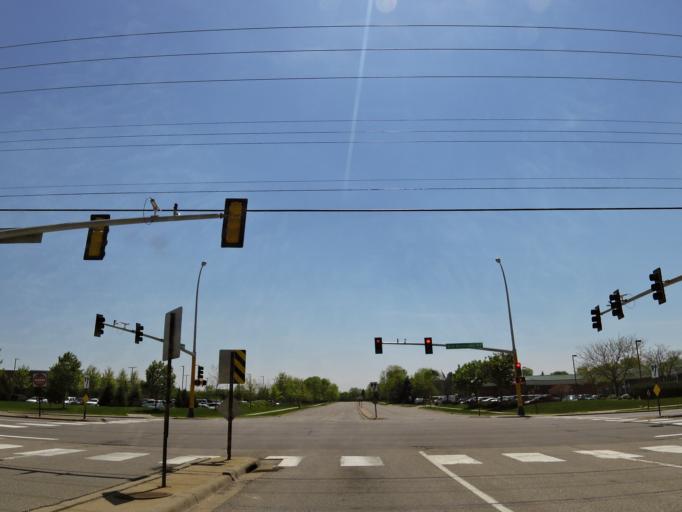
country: US
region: Minnesota
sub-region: Scott County
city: Savage
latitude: 44.8082
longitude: -93.3768
